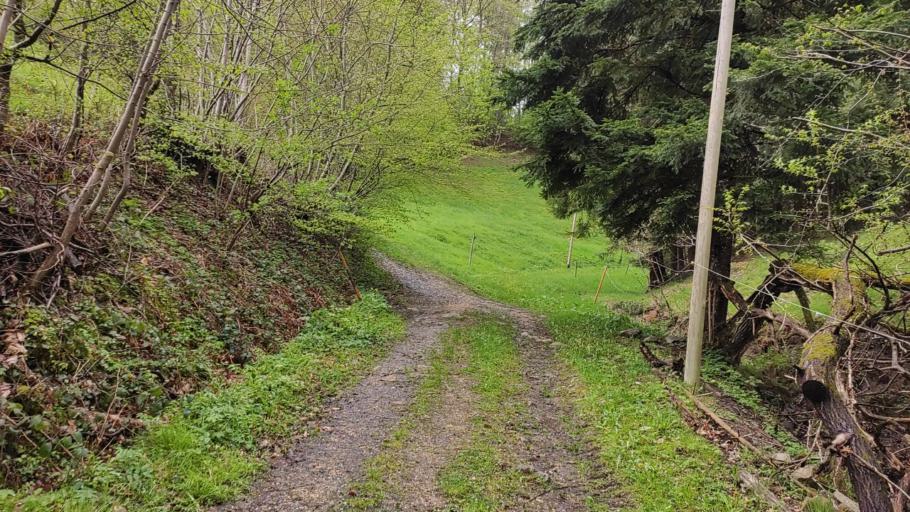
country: DE
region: Baden-Wuerttemberg
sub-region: Freiburg Region
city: Solden
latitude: 47.9100
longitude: 7.8356
